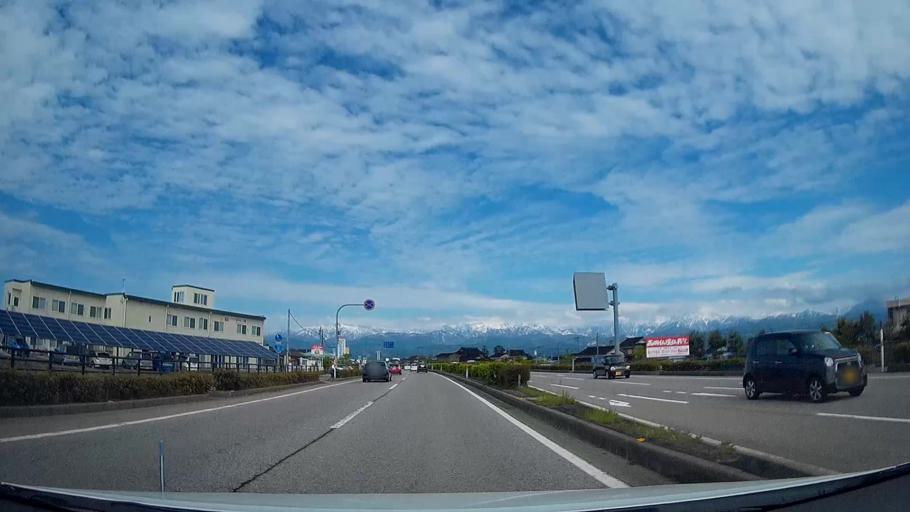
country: JP
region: Toyama
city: Namerikawa
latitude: 36.7179
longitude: 137.2912
